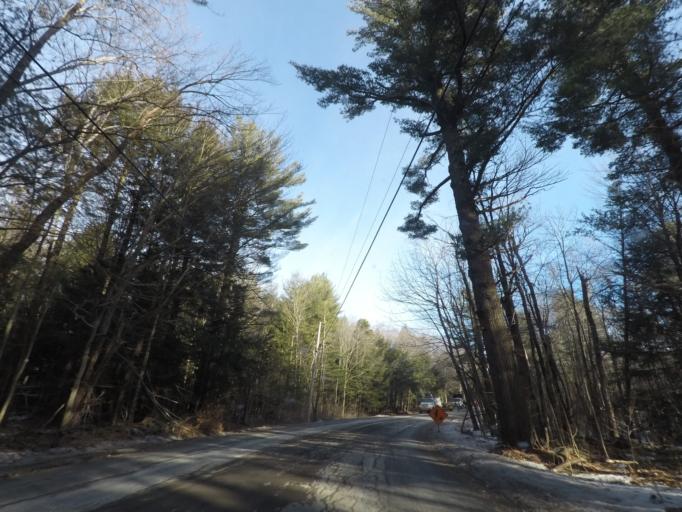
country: US
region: New York
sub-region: Rensselaer County
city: Hoosick Falls
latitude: 42.7405
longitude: -73.3956
